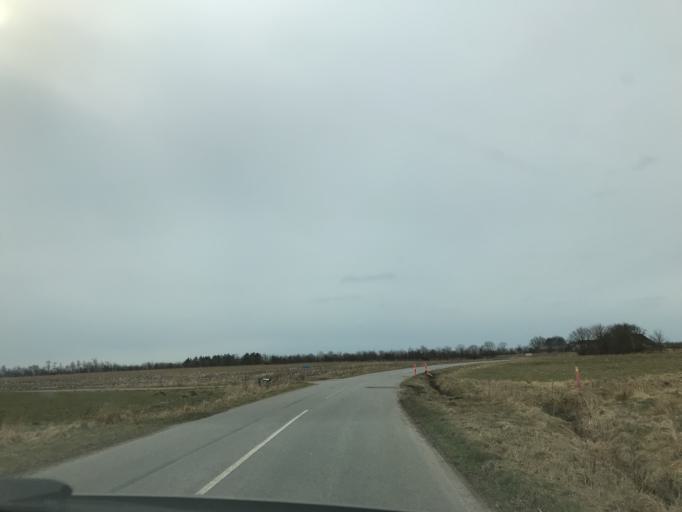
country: DK
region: South Denmark
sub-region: Varde Kommune
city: Oksbol
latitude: 55.8036
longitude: 8.3599
